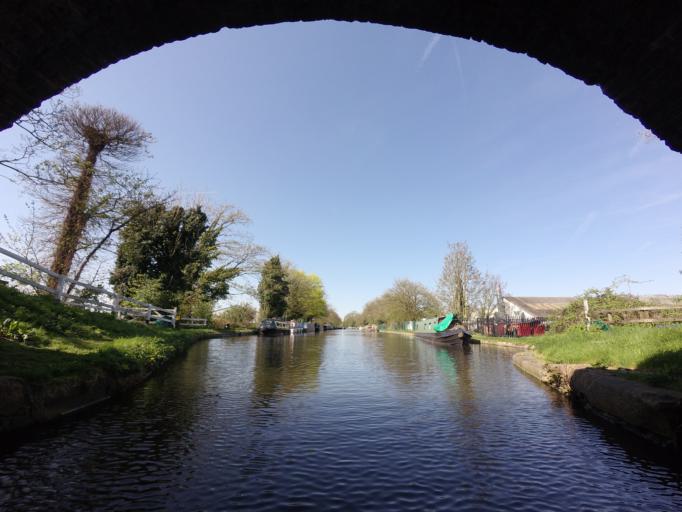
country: GB
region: England
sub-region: Greater London
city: Uxbridge
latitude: 51.5298
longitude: -0.4859
